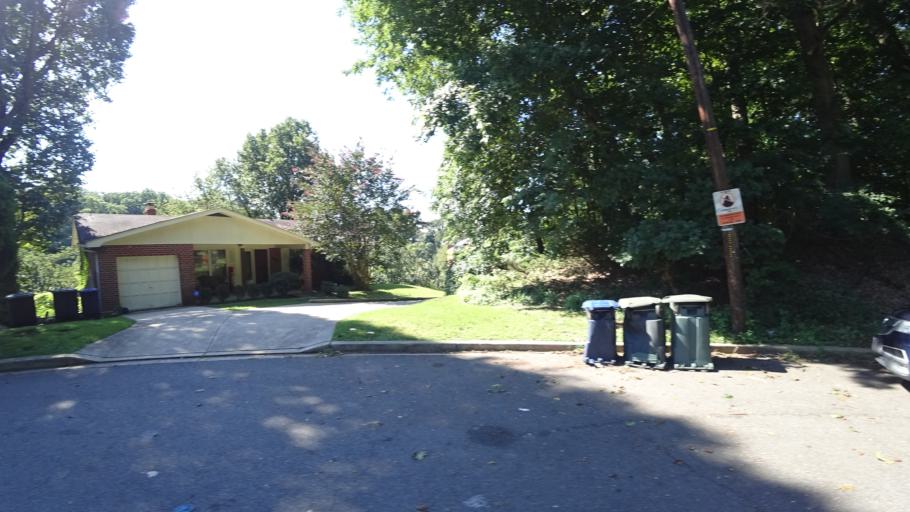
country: US
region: Maryland
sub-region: Montgomery County
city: Chevy Chase
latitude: 38.9439
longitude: -77.0456
